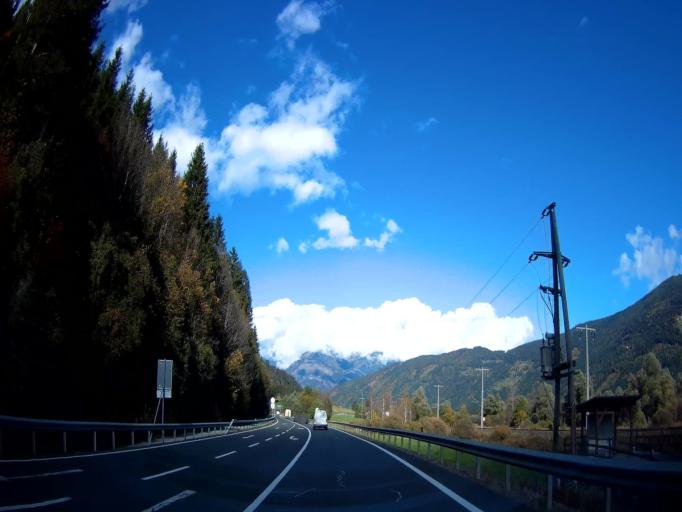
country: AT
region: Carinthia
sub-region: Politischer Bezirk Spittal an der Drau
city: Sachsenburg
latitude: 46.7748
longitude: 13.3437
